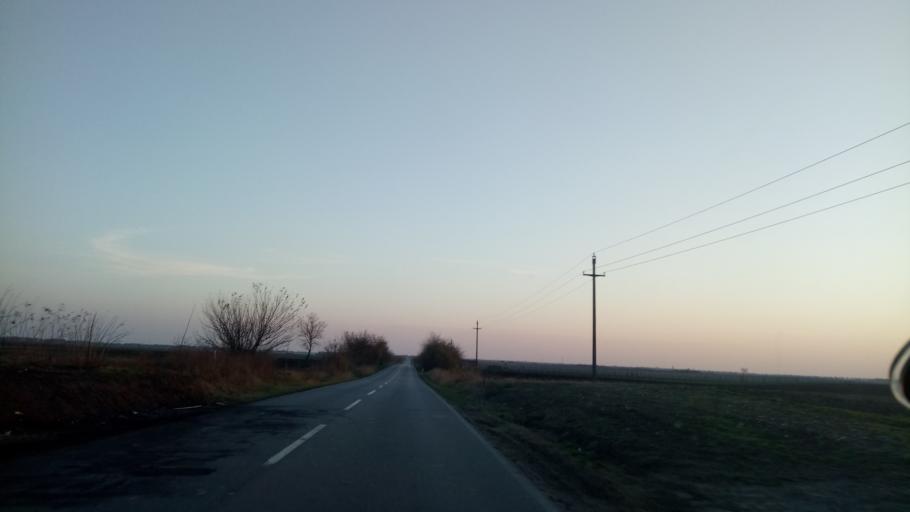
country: RS
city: Surduk
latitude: 45.0491
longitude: 20.3323
